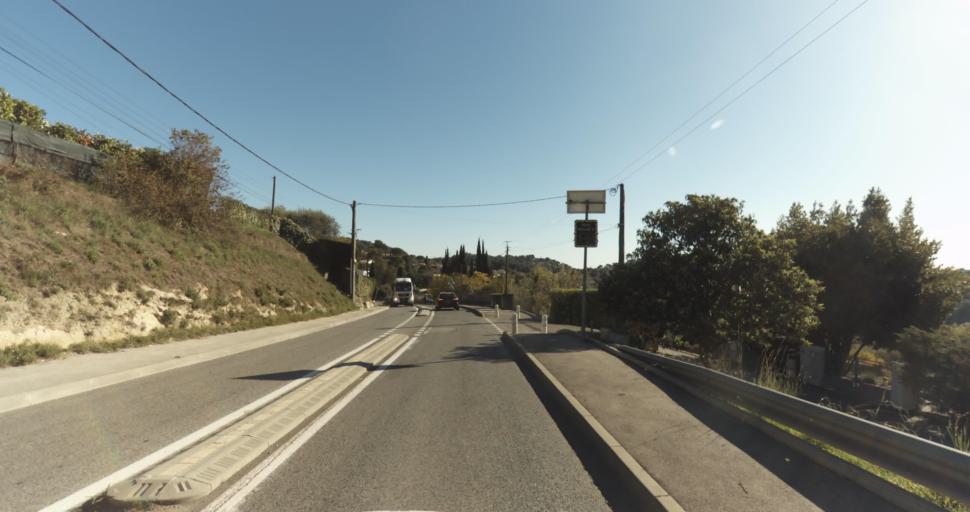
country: FR
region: Provence-Alpes-Cote d'Azur
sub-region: Departement des Alpes-Maritimes
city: Vence
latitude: 43.7130
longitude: 7.1217
